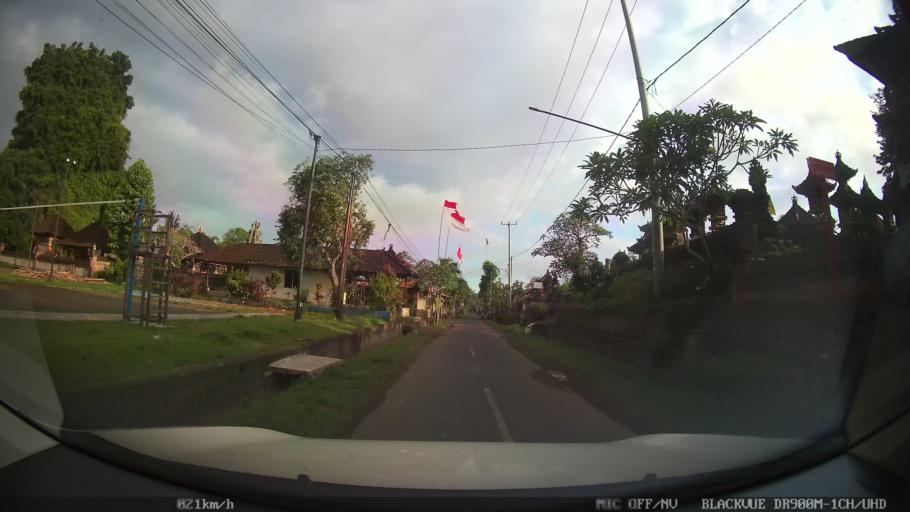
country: ID
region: Bali
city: Banjar Tebongkang
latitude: -8.5357
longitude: 115.2522
